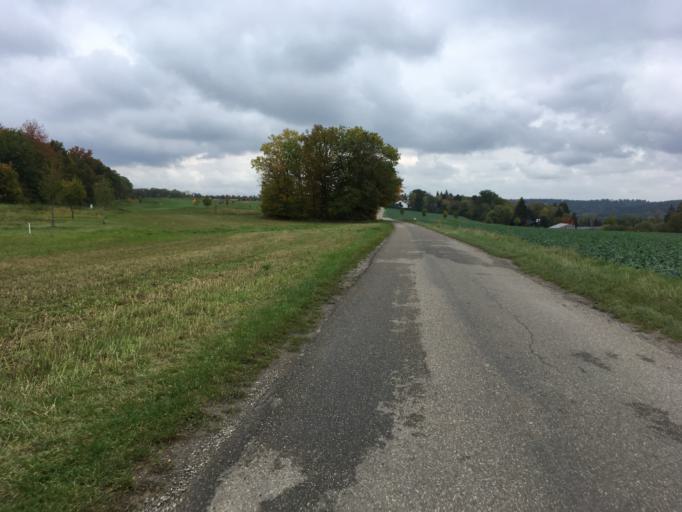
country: DE
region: Baden-Wuerttemberg
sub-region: Tuebingen Region
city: Dusslingen
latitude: 48.4747
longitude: 9.0506
